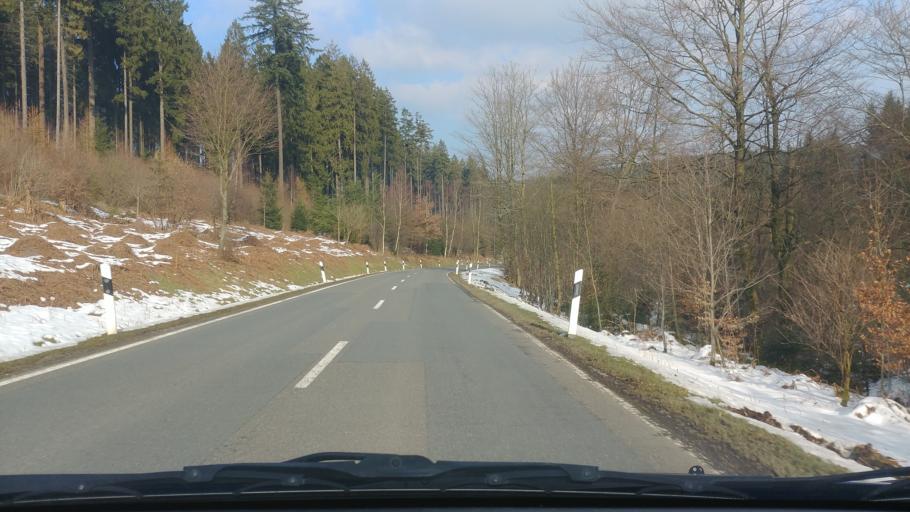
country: DE
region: Lower Saxony
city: Uslar
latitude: 51.7294
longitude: 9.6302
